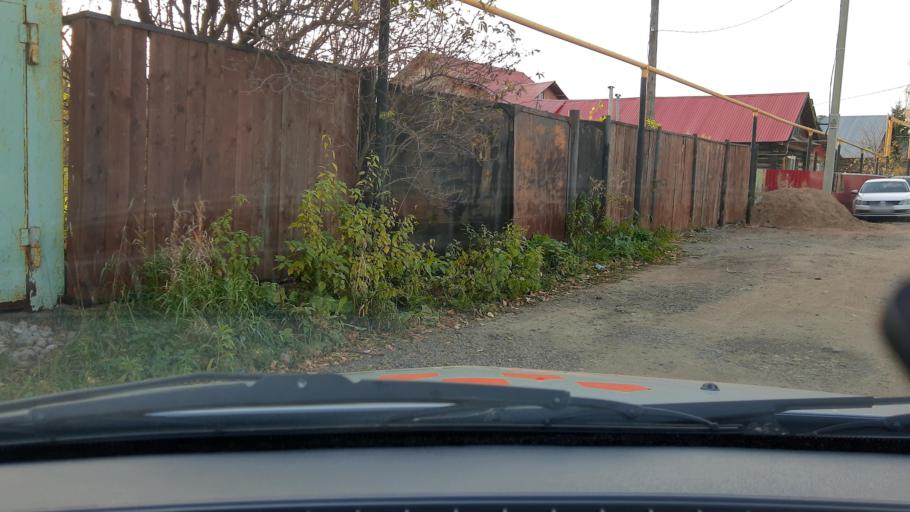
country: RU
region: Bashkortostan
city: Ufa
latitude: 54.8276
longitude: 56.1317
